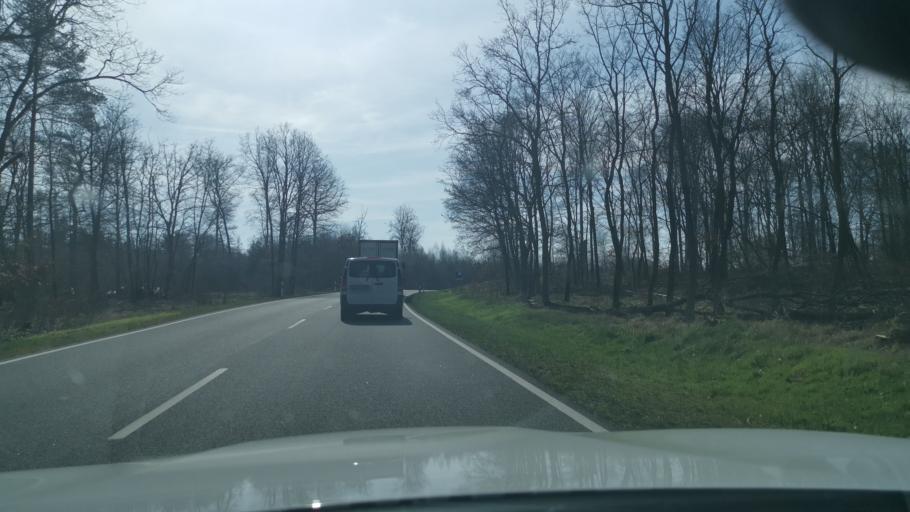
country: DE
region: Saxony-Anhalt
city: Kemberg
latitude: 51.6843
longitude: 12.6119
